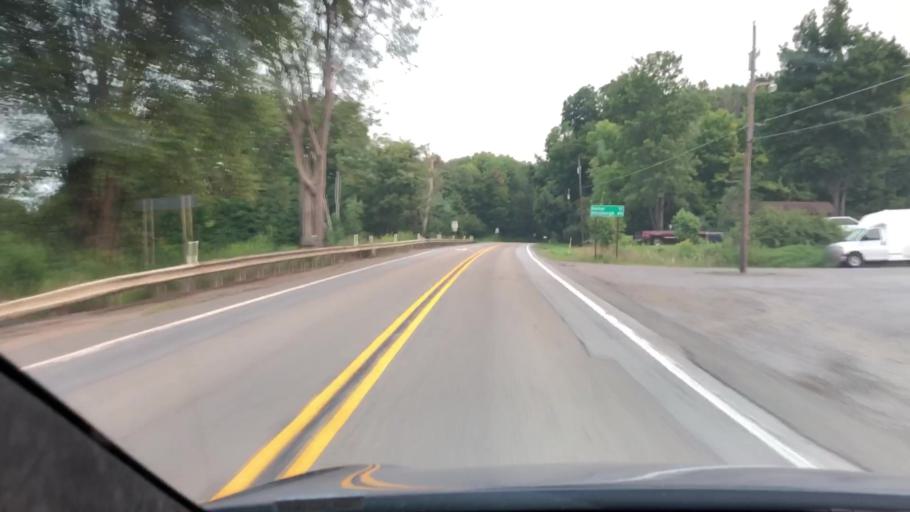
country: US
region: Pennsylvania
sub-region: Butler County
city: Slippery Rock
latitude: 41.0928
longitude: -80.0022
